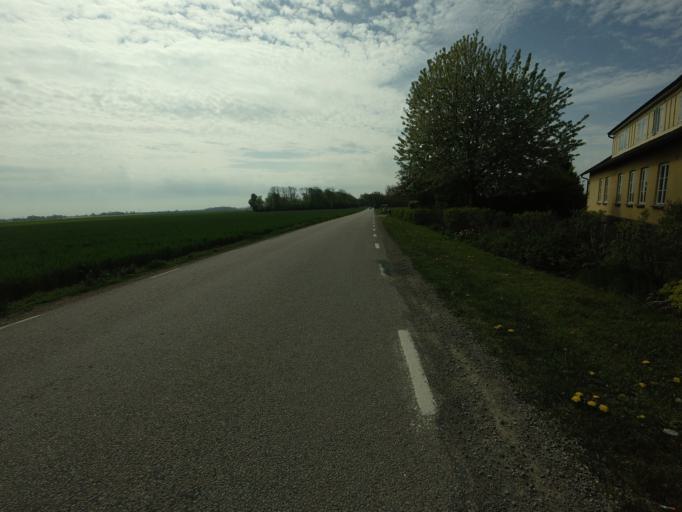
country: SE
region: Skane
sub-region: Hoganas Kommun
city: Hoganas
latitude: 56.2456
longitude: 12.5733
